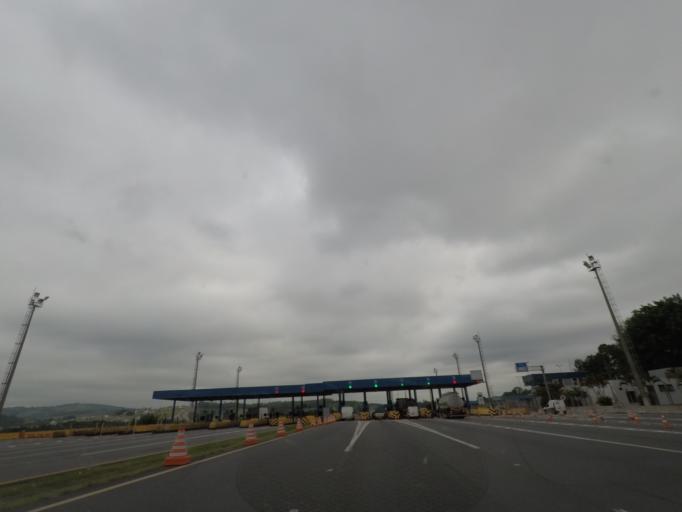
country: BR
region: Sao Paulo
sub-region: Itatiba
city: Itatiba
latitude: -22.9535
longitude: -46.8606
